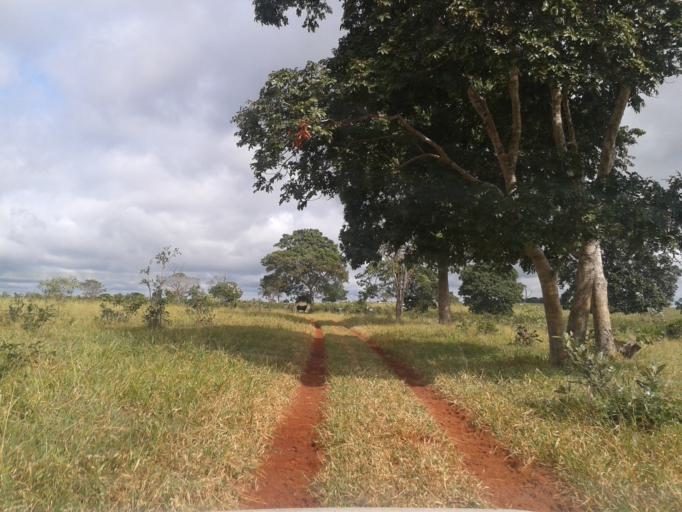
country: BR
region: Minas Gerais
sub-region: Campina Verde
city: Campina Verde
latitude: -19.4139
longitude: -49.6741
